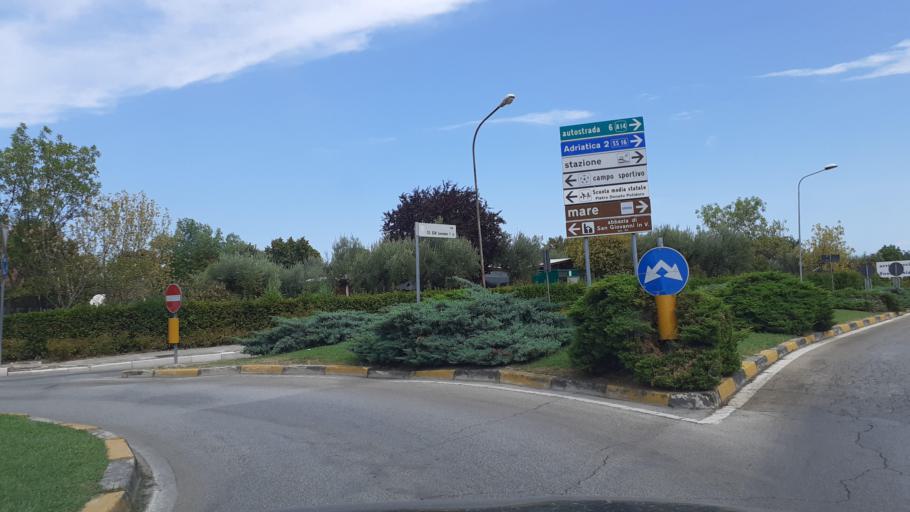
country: IT
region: Abruzzo
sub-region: Provincia di Chieti
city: Fossacesia
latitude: 42.2477
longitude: 14.4850
